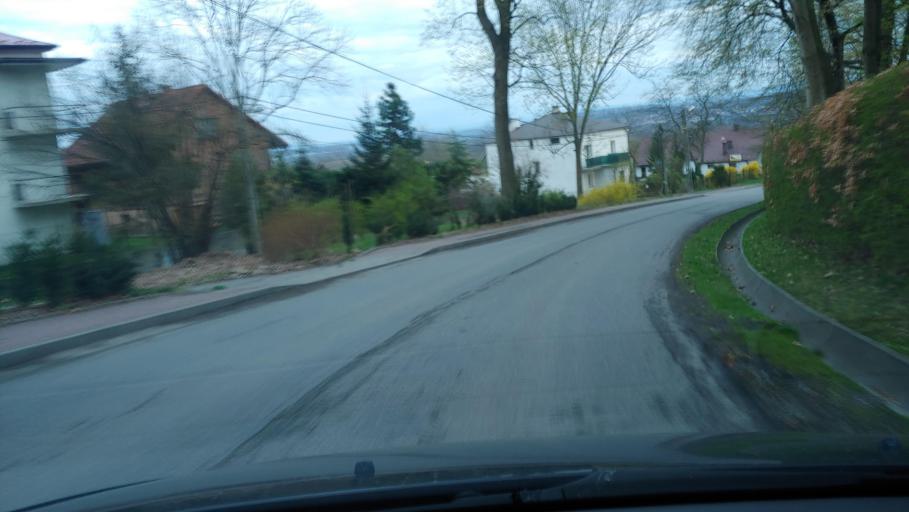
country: PL
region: Lesser Poland Voivodeship
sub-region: Powiat krakowski
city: Bolechowice
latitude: 50.1523
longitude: 19.7779
